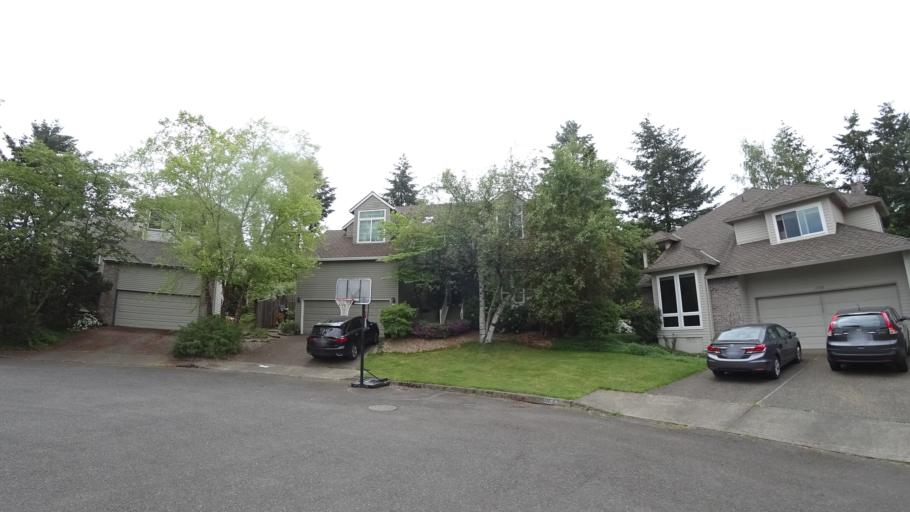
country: US
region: Oregon
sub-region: Clackamas County
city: Lake Oswego
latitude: 45.4406
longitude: -122.7059
